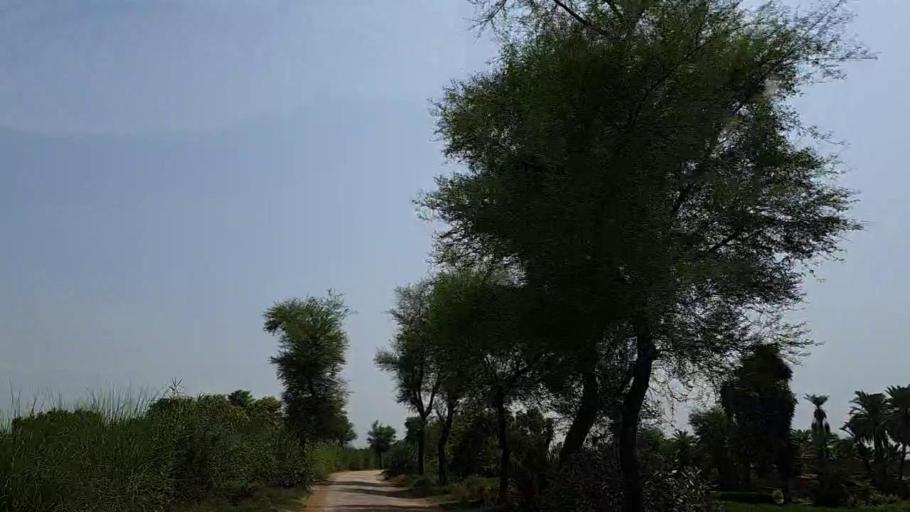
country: PK
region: Sindh
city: Adilpur
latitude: 27.9093
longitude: 69.3647
